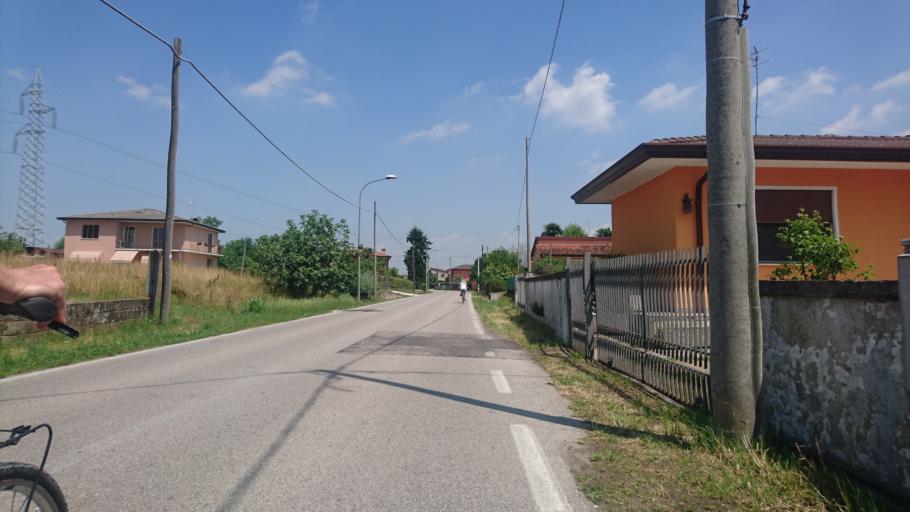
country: IT
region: Veneto
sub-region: Provincia di Venezia
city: Galta
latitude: 45.3880
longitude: 12.0250
